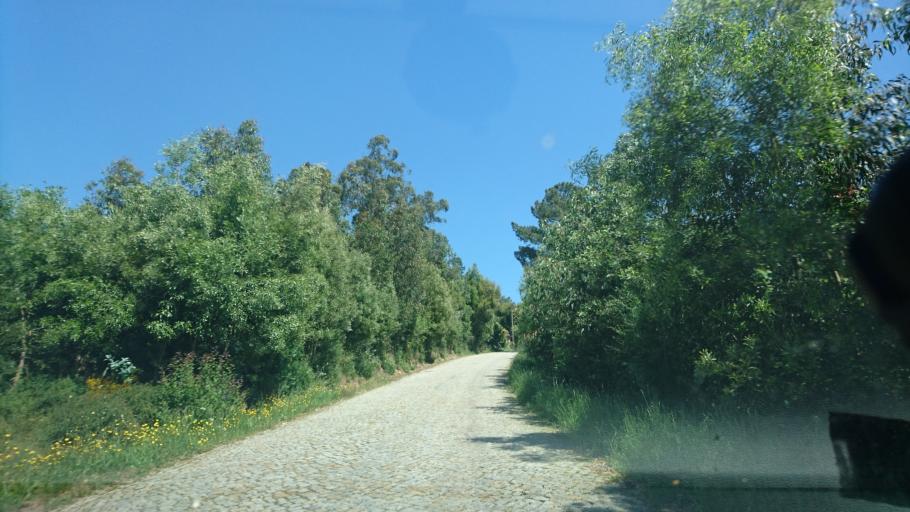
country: PT
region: Porto
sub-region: Paredes
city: Recarei
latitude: 41.1399
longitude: -8.3813
